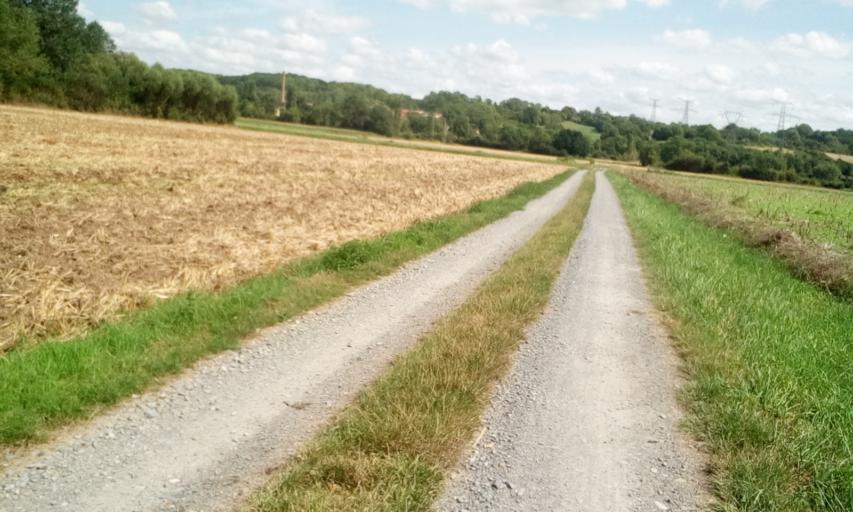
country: FR
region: Lower Normandy
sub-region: Departement du Calvados
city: Argences
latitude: 49.1368
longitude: -0.1738
